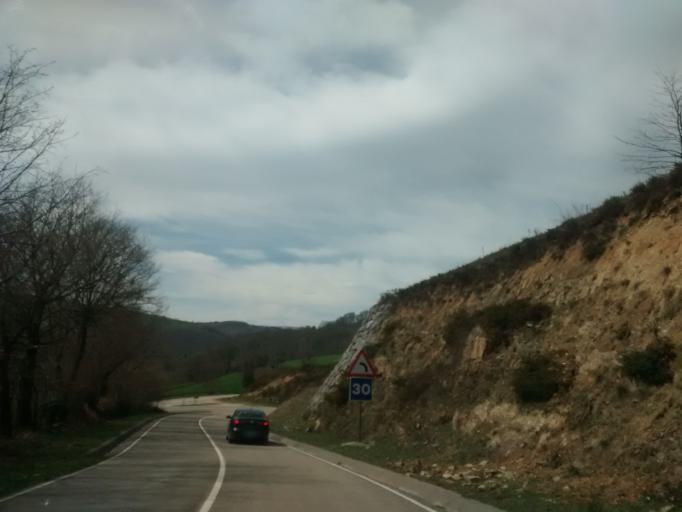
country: ES
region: Cantabria
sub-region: Provincia de Cantabria
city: Vega de Pas
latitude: 43.1638
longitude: -3.7930
